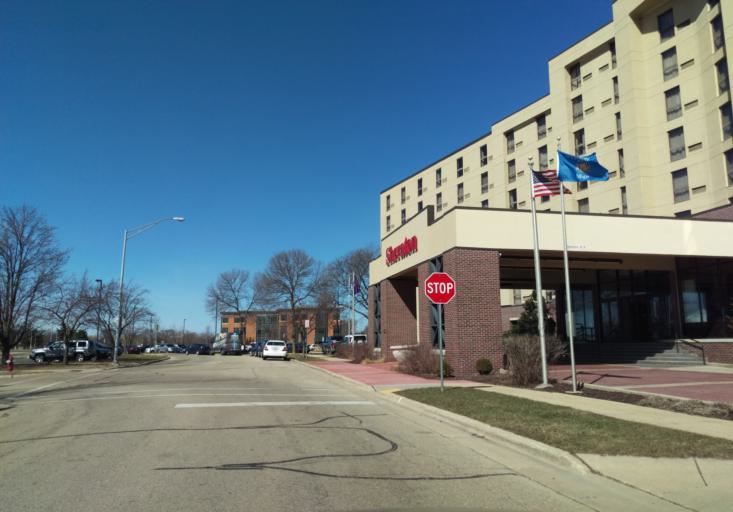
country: US
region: Wisconsin
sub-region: Dane County
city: Madison
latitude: 43.0471
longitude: -89.3733
